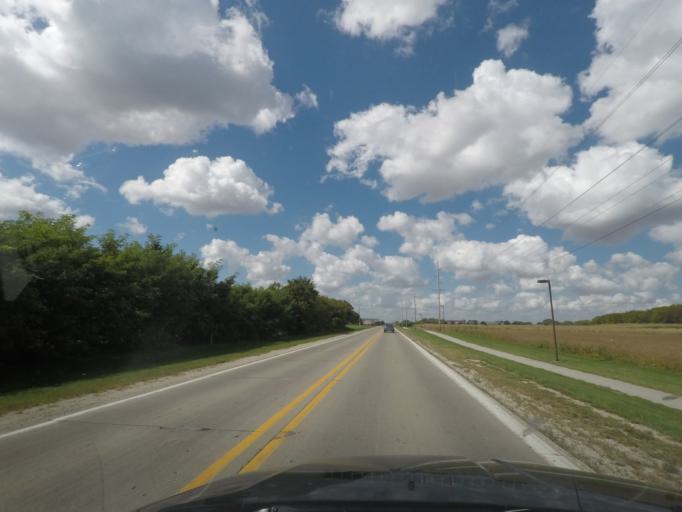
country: US
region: Iowa
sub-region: Story County
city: Ames
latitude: 42.0119
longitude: -93.6622
